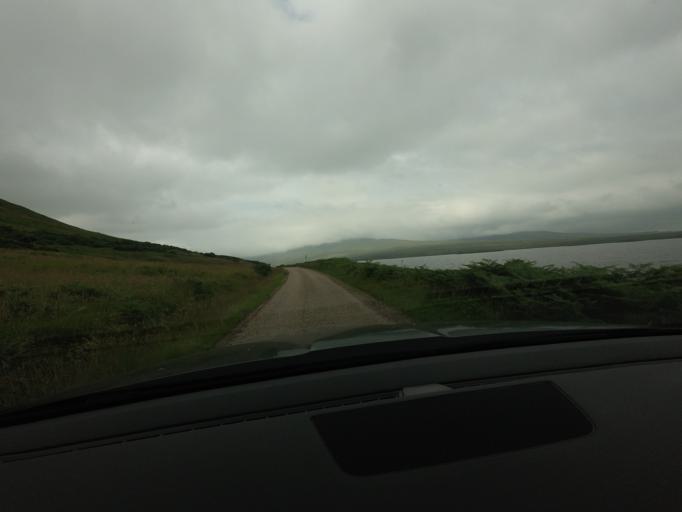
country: GB
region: Scotland
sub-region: Highland
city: Golspie
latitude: 58.3769
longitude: -4.3662
